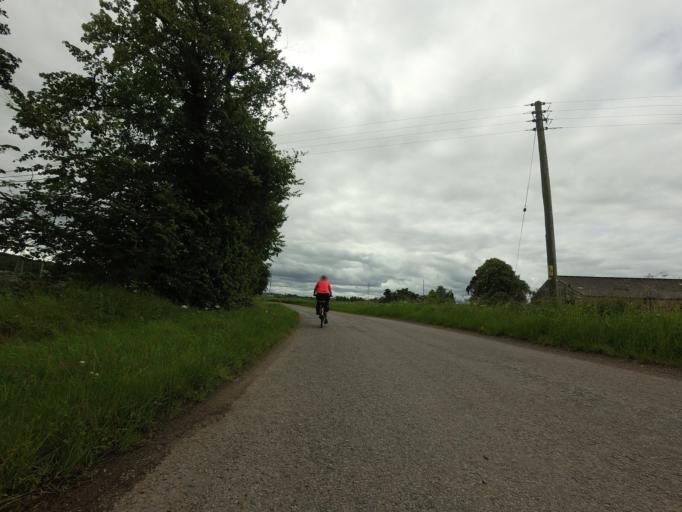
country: GB
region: Scotland
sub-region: Moray
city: Forres
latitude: 57.6219
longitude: -3.6137
